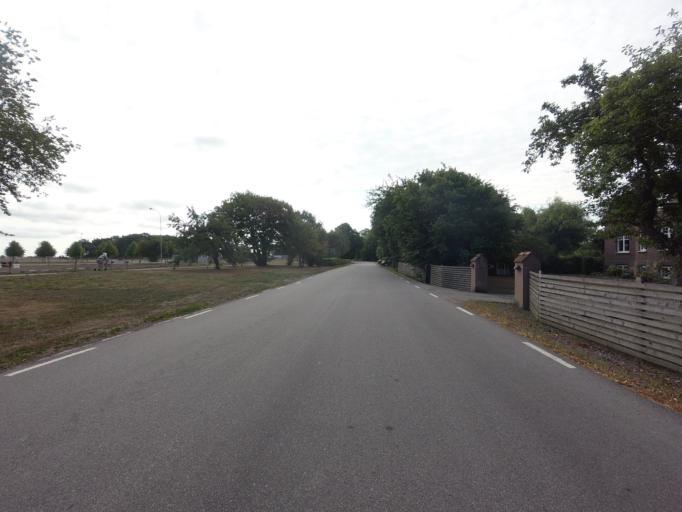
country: SE
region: Skane
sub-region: Helsingborg
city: Odakra
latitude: 56.1770
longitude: 12.6780
